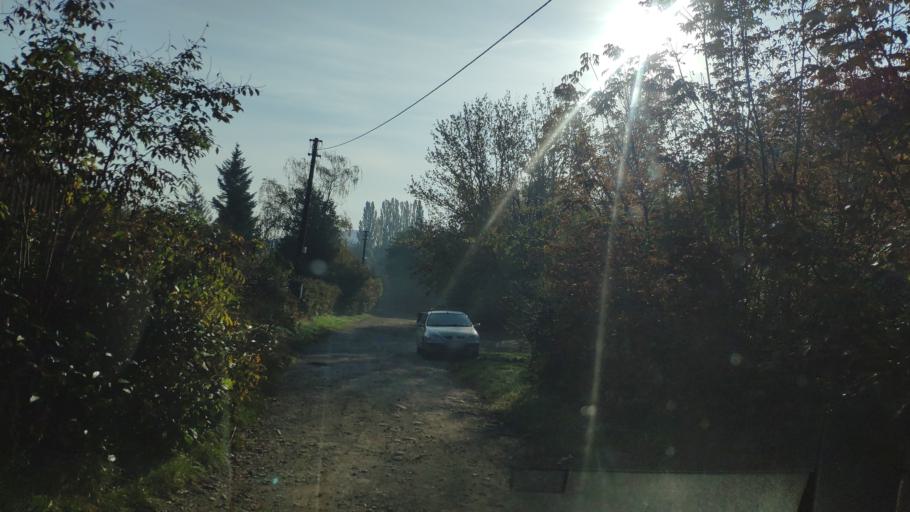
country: SK
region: Kosicky
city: Kosice
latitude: 48.7251
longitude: 21.2267
